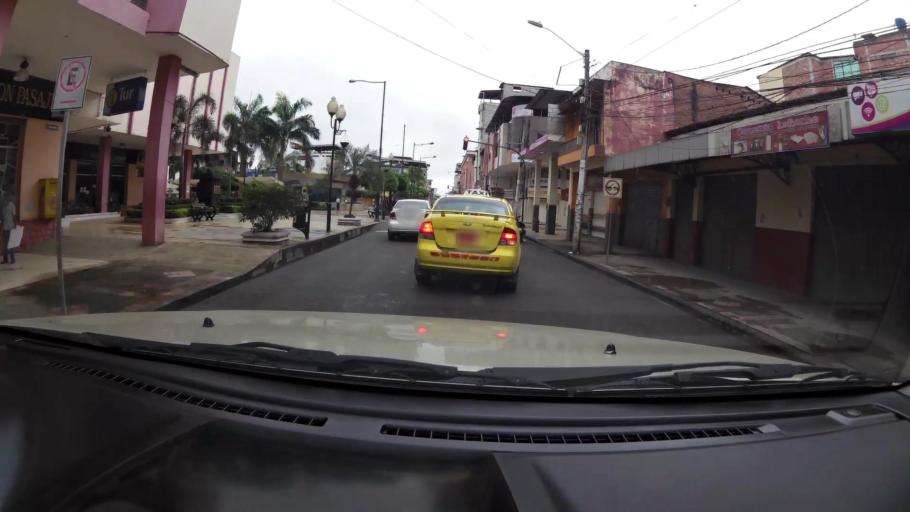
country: EC
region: El Oro
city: Pasaje
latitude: -3.3282
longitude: -79.8078
